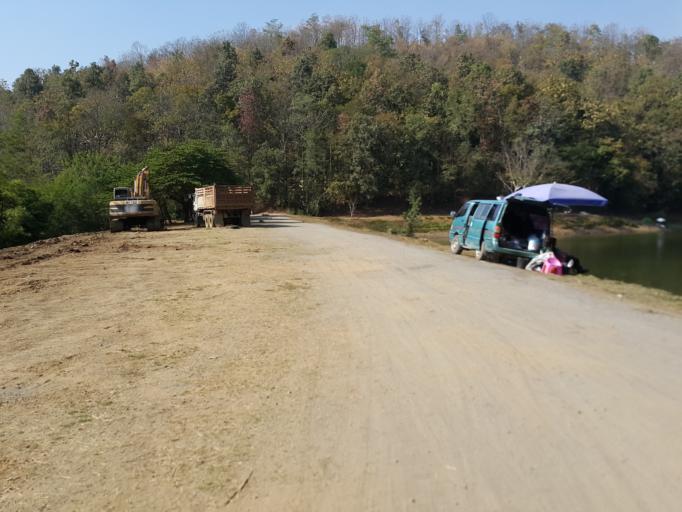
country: TH
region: Chiang Mai
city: Mae On
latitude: 18.8347
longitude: 99.2360
